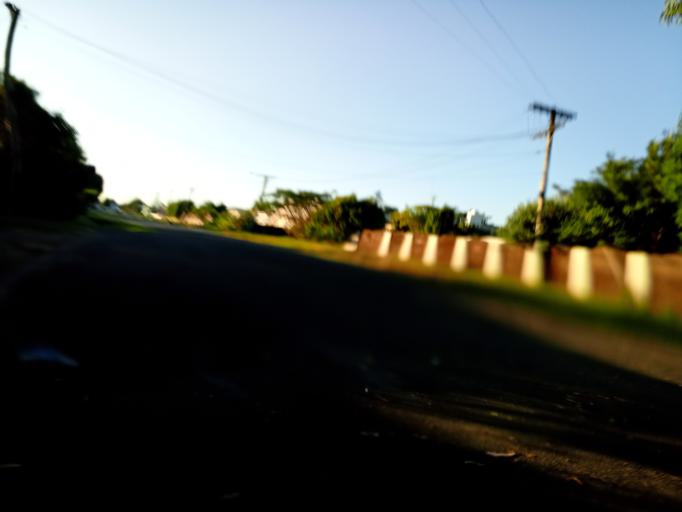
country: NZ
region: Gisborne
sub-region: Gisborne District
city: Gisborne
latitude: -38.6502
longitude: 178.0131
